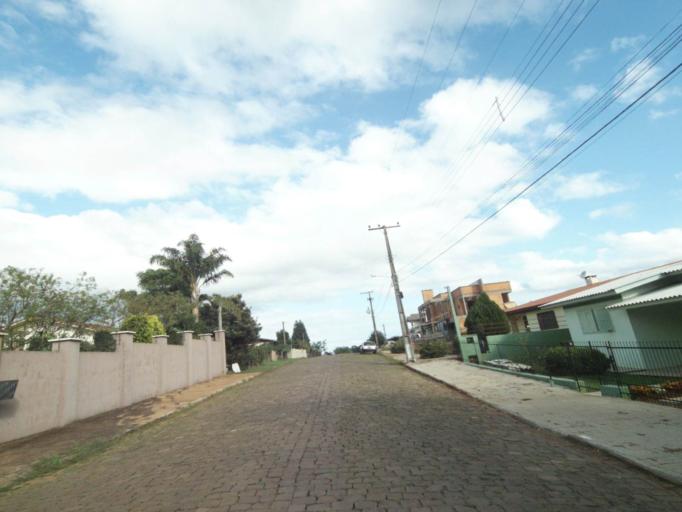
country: BR
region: Rio Grande do Sul
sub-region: Lagoa Vermelha
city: Lagoa Vermelha
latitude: -28.2061
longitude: -51.5161
